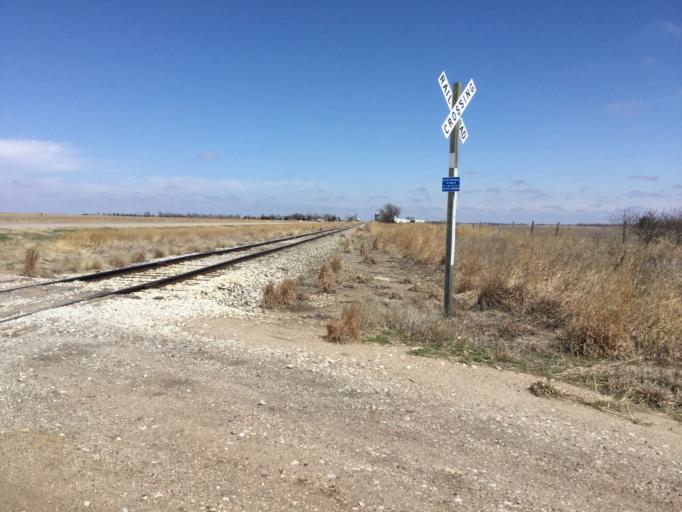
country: US
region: Kansas
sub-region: Barton County
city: Great Bend
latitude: 38.3016
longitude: -98.9034
